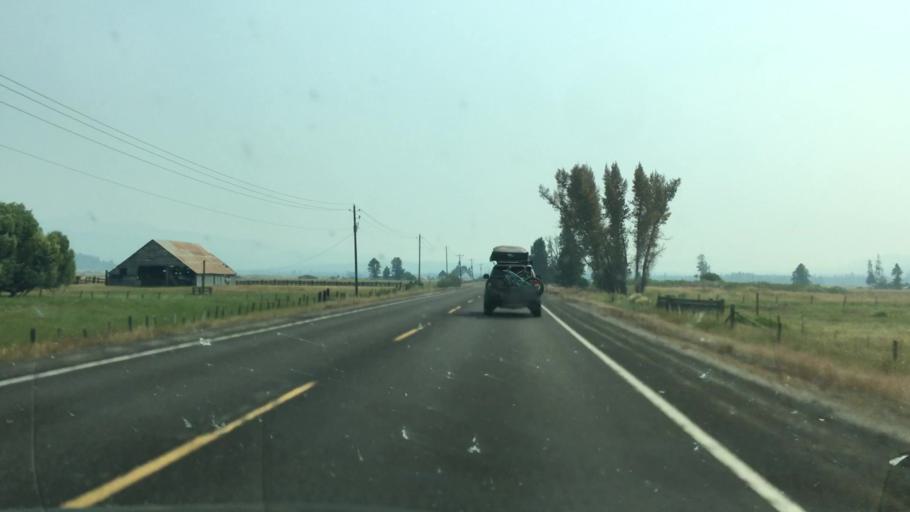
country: US
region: Idaho
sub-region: Valley County
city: Cascade
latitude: 44.4333
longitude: -115.9994
